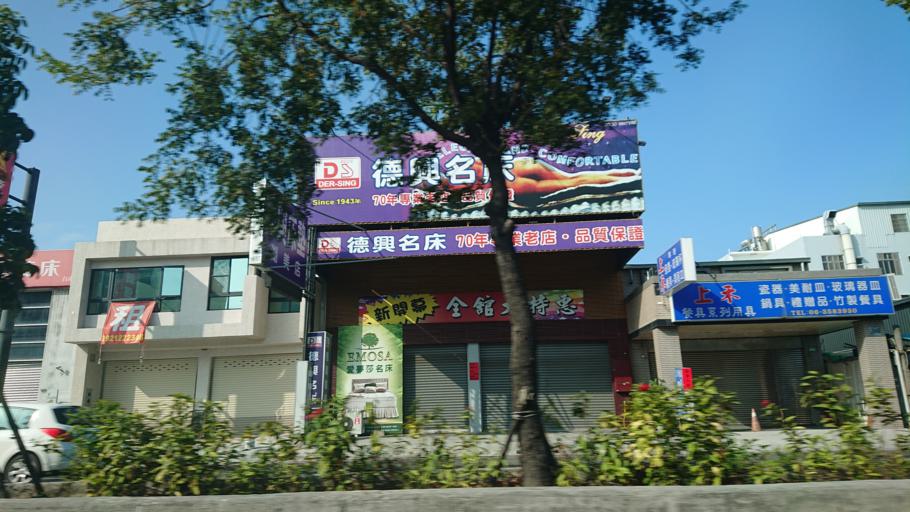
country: TW
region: Taiwan
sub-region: Tainan
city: Tainan
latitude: 23.0093
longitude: 120.1856
